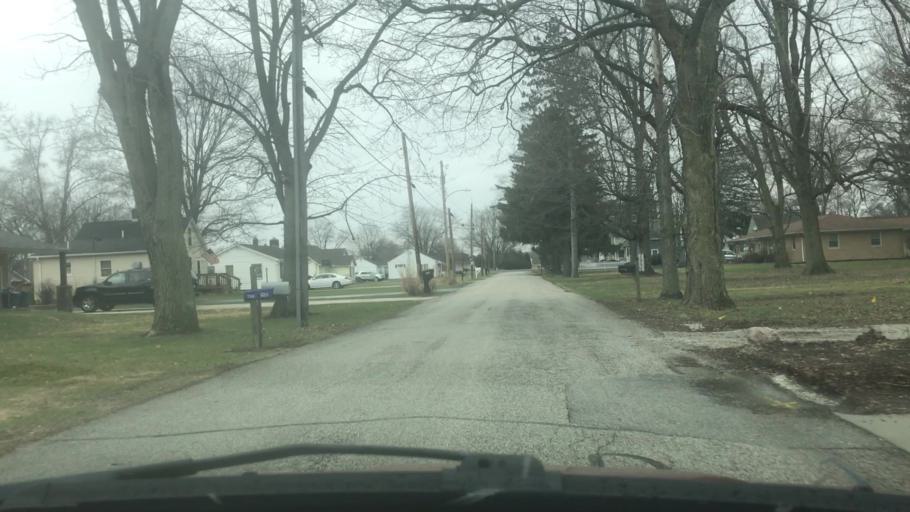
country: US
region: Indiana
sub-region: Porter County
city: Kouts
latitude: 41.3207
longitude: -87.0238
